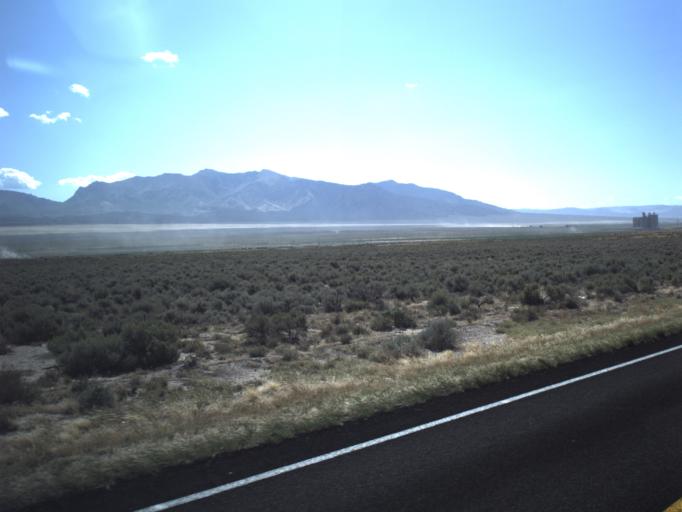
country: US
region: Utah
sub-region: Beaver County
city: Milford
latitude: 38.4169
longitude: -113.0099
